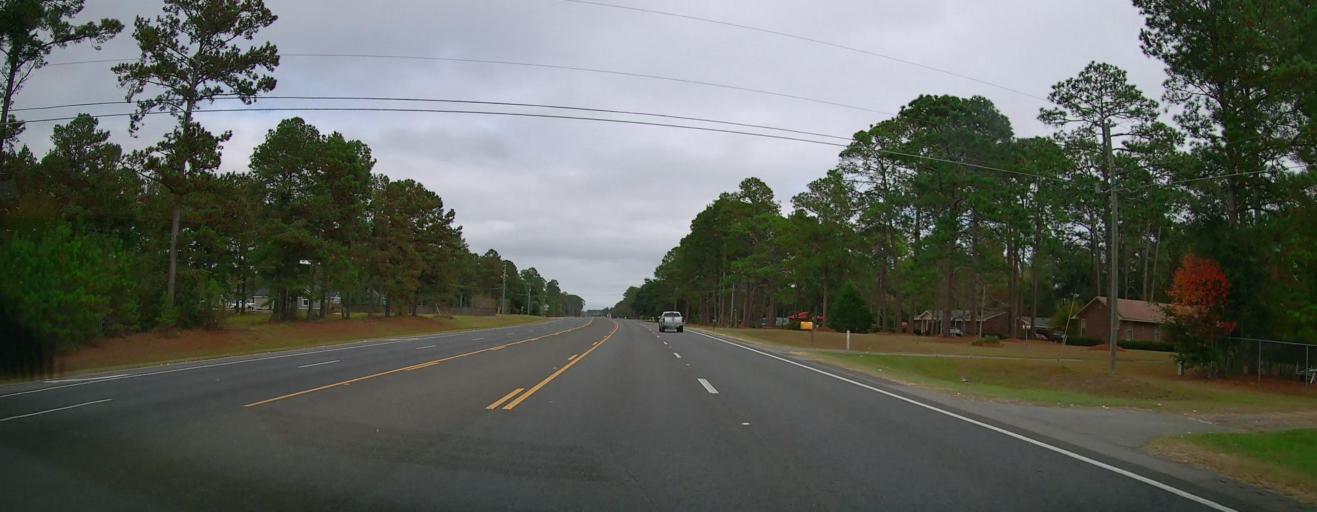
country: US
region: Georgia
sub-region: Colquitt County
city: Moultrie
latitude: 31.0932
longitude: -83.8045
